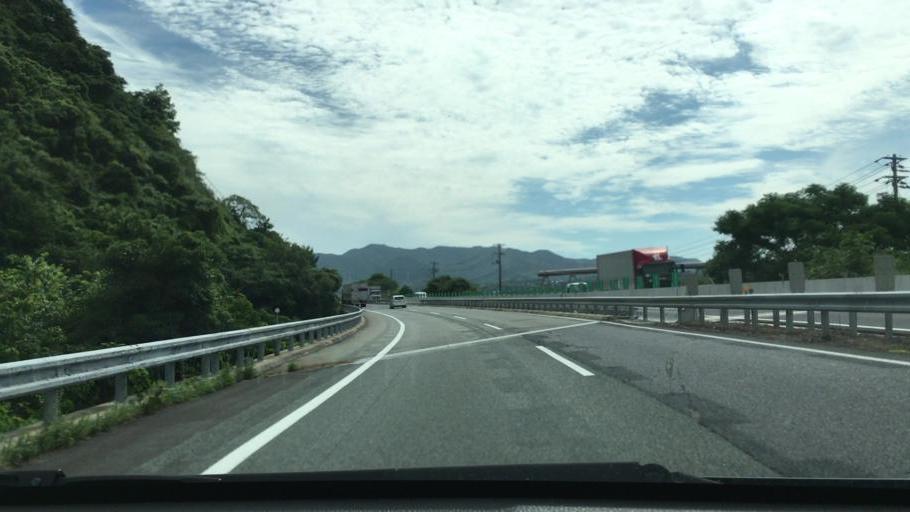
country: JP
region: Yamaguchi
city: Ogori-shimogo
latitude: 34.1325
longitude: 131.4273
